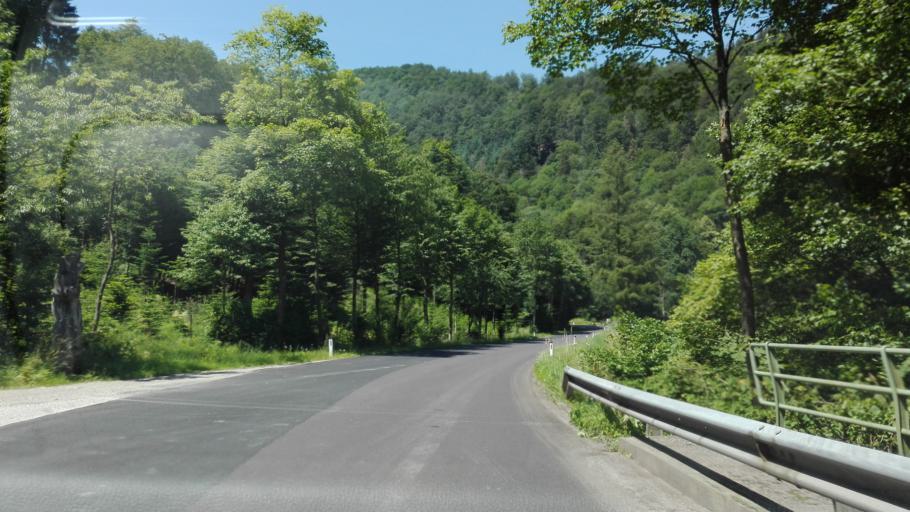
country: AT
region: Upper Austria
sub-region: Politischer Bezirk Rohrbach
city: Kleinzell im Muehlkreis
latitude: 48.3748
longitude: 13.9417
